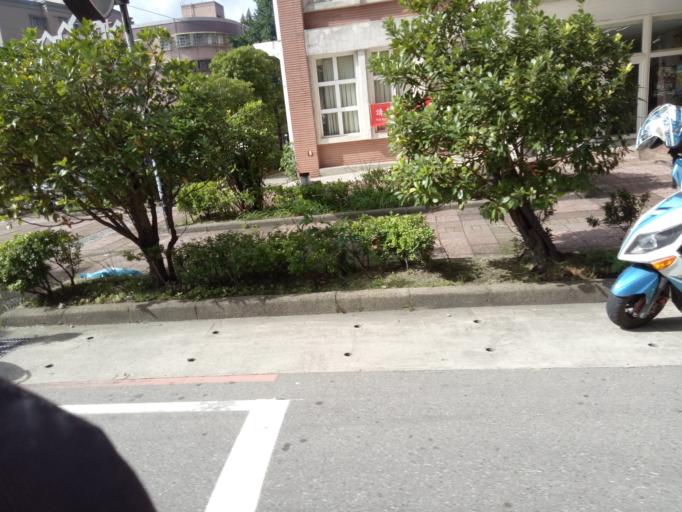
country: TW
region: Taiwan
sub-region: Taoyuan
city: Taoyuan
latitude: 24.9422
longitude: 121.3391
